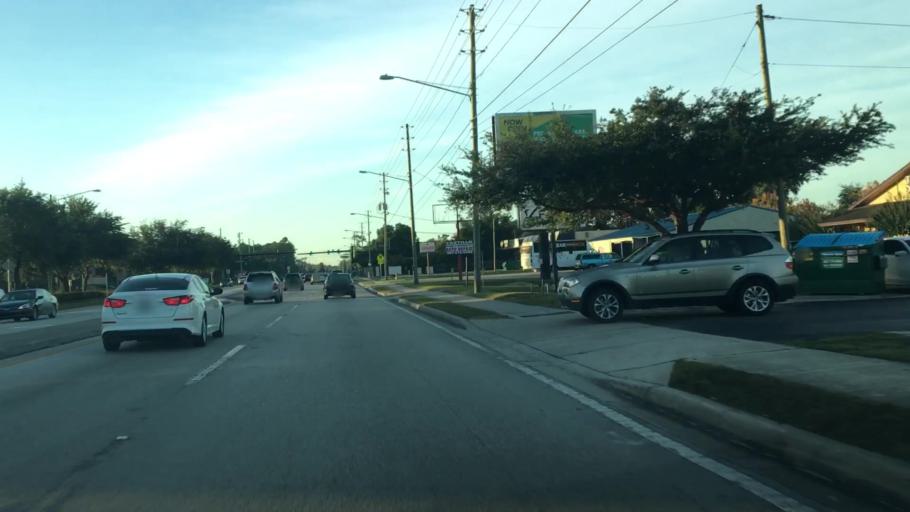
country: US
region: Florida
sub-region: Orange County
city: Conway
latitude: 28.4903
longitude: -81.2855
